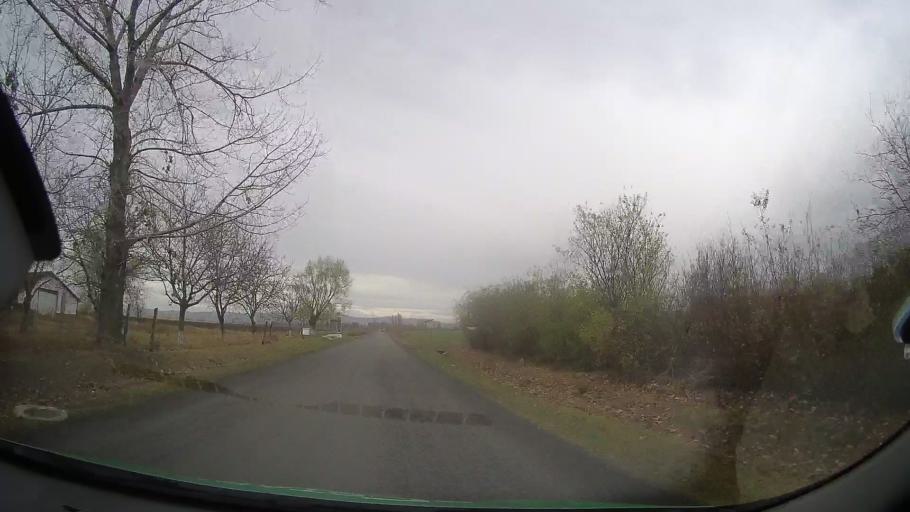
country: RO
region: Prahova
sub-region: Comuna Colceag
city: Inotesti
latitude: 44.9636
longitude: 26.3482
